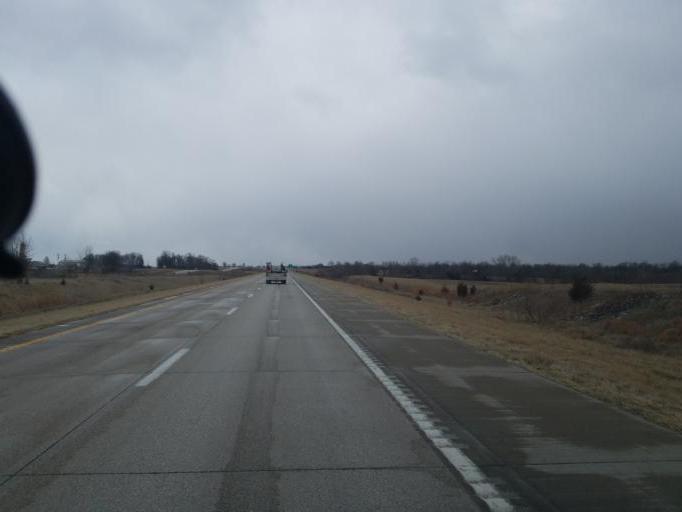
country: US
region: Missouri
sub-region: Randolph County
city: Moberly
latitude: 39.4760
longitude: -92.4348
